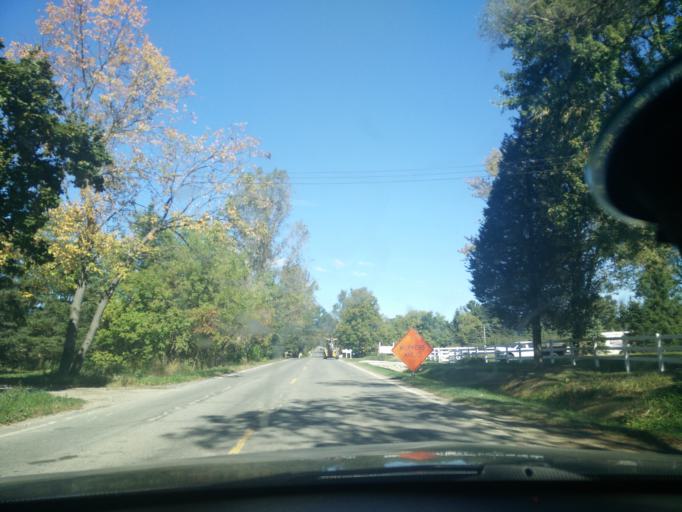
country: US
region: Michigan
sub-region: Oakland County
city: South Lyon
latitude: 42.4216
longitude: -83.5896
